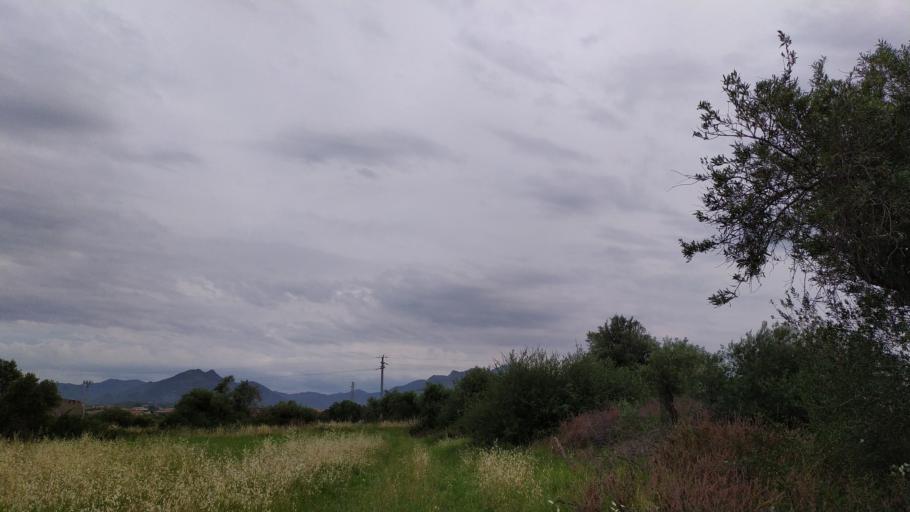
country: IT
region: Sicily
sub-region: Messina
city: San Filippo del Mela
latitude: 38.1843
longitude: 15.2629
